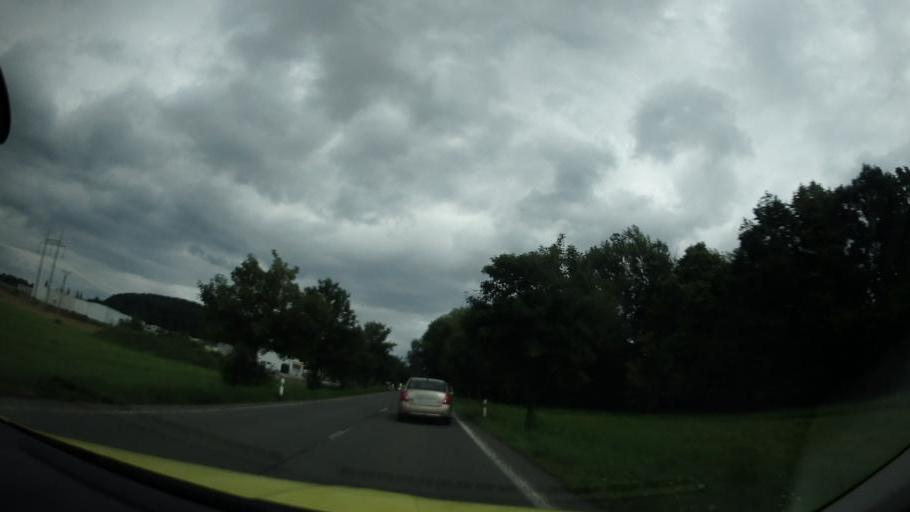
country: CZ
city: Verovice
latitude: 49.5414
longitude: 18.0911
